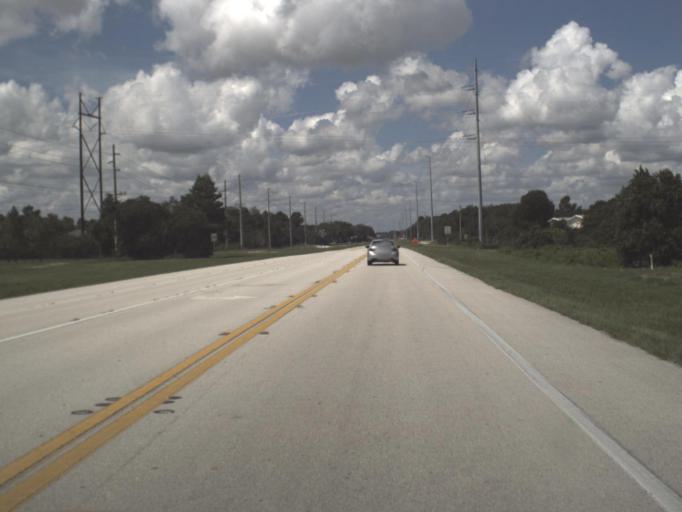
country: US
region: Florida
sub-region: Polk County
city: Gibsonia
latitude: 28.1108
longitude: -81.9196
